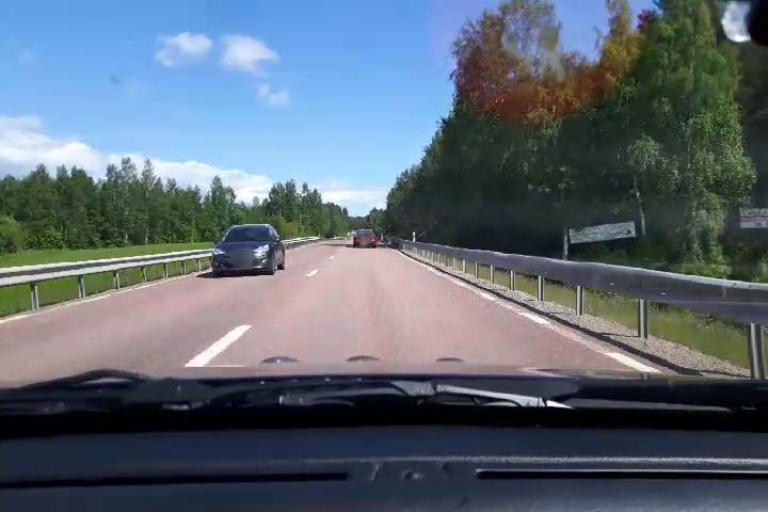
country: SE
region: Gaevleborg
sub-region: Hudiksvalls Kommun
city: Delsbo
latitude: 61.7974
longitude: 16.5079
